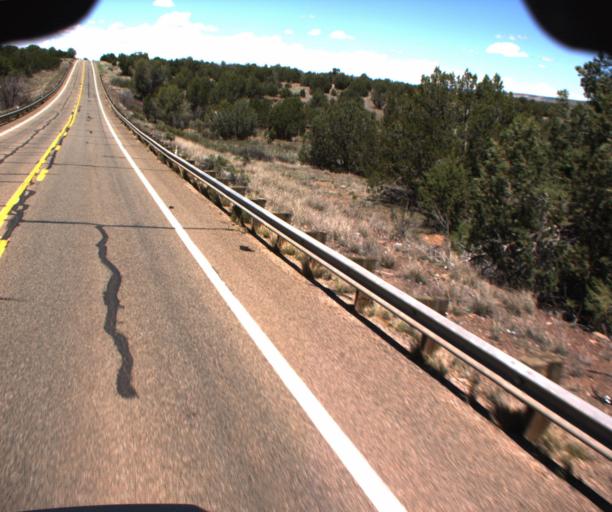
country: US
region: Arizona
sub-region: Coconino County
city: Williams
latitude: 35.1983
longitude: -112.4729
